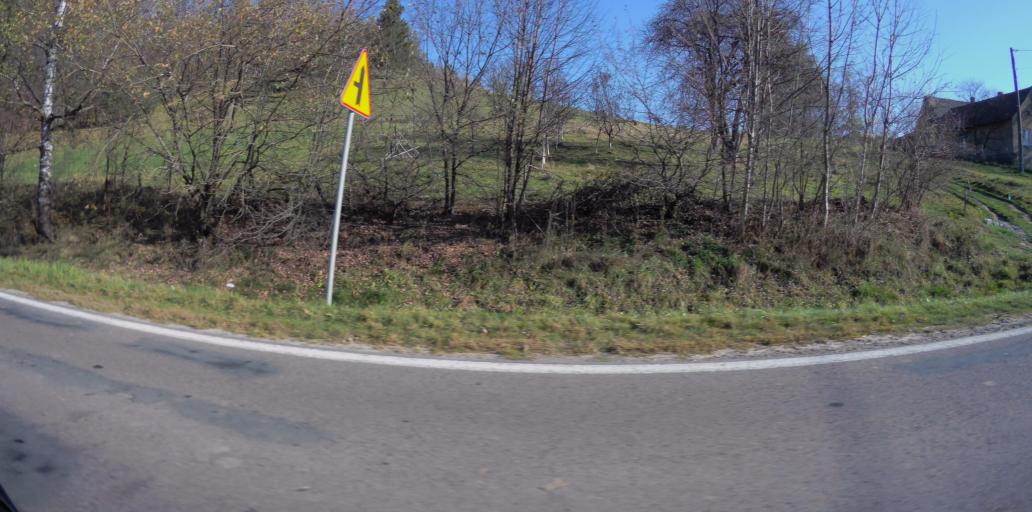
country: PL
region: Subcarpathian Voivodeship
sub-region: Powiat bieszczadzki
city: Ustrzyki Dolne
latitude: 49.5296
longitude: 22.6020
